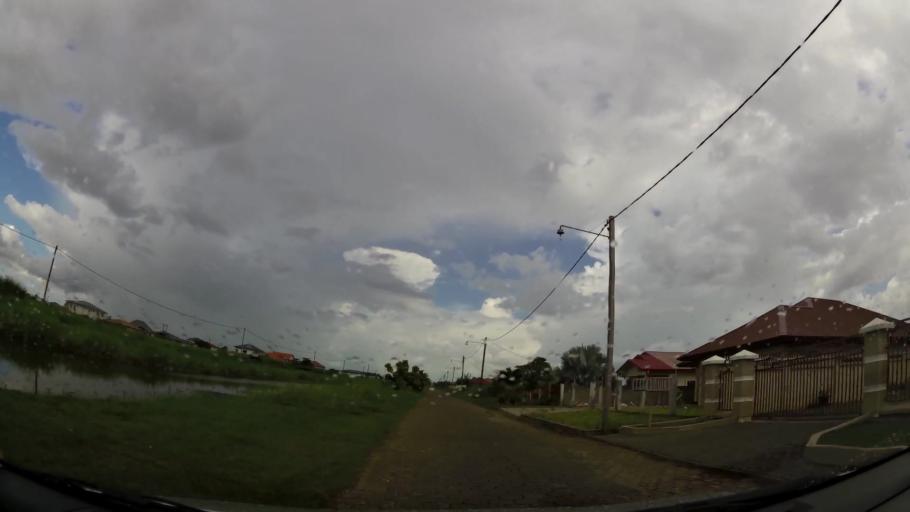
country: SR
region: Commewijne
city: Nieuw Amsterdam
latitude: 5.8645
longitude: -55.1177
